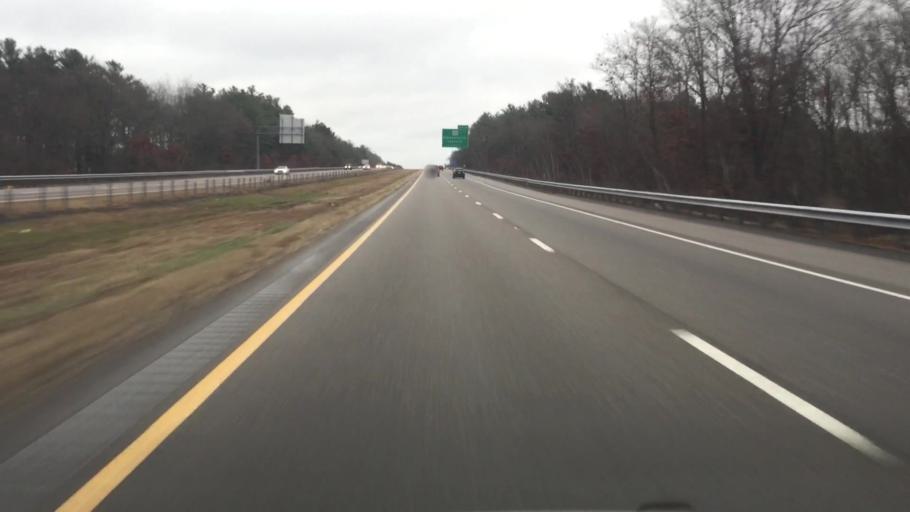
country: US
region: Massachusetts
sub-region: Plymouth County
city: Middleborough Center
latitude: 41.8887
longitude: -70.9364
